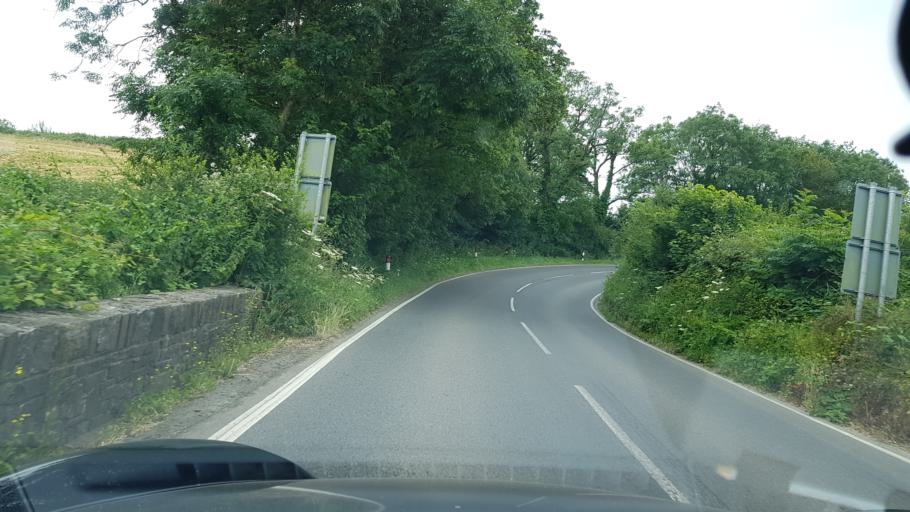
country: GB
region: Wales
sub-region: Pembrokeshire
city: Haverfordwest
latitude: 51.7912
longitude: -5.0038
